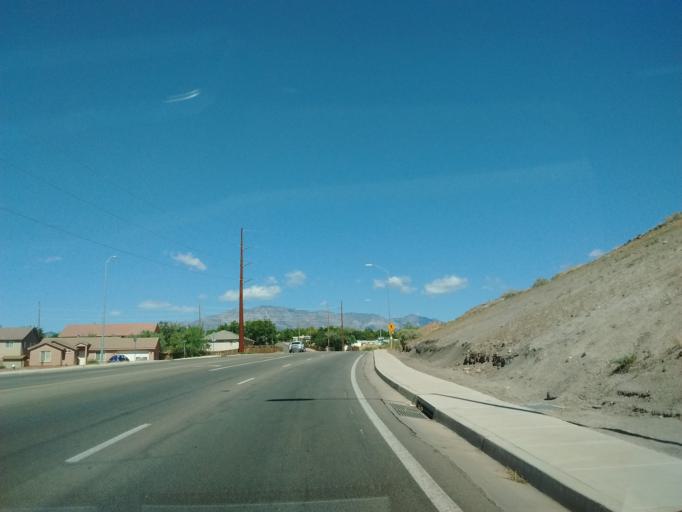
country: US
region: Utah
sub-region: Washington County
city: Washington
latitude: 37.1258
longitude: -113.5052
